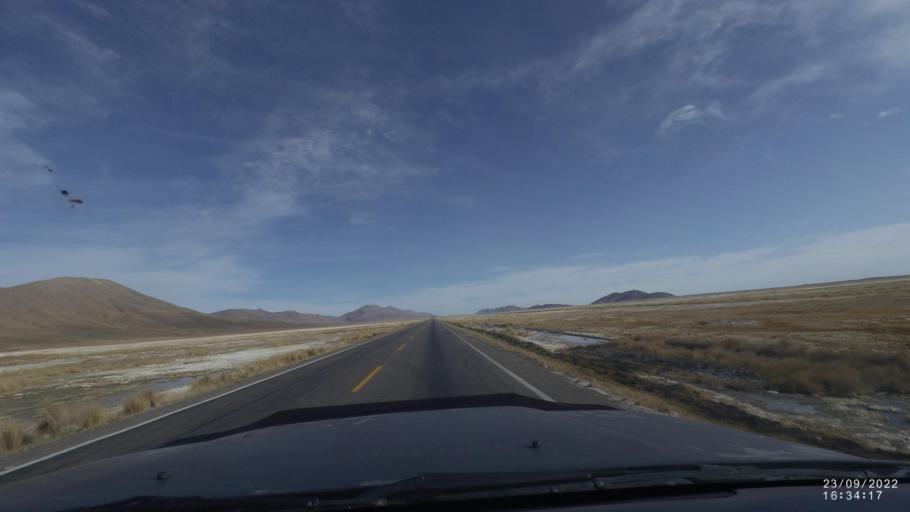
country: BO
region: Oruro
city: Machacamarca
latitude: -18.1866
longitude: -67.0149
